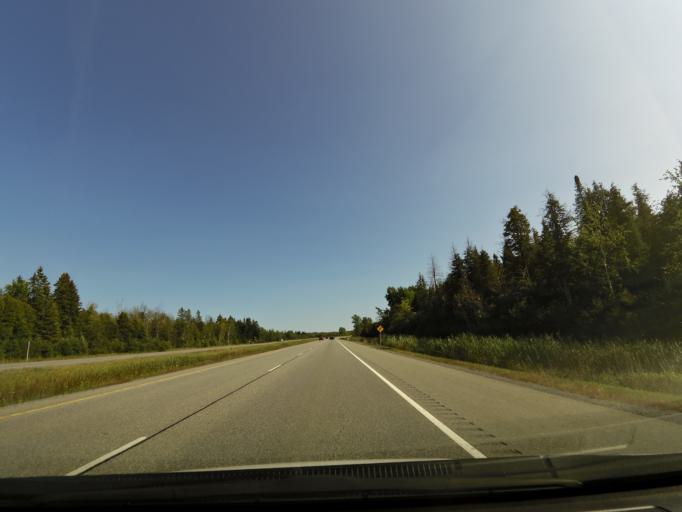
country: CA
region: Ontario
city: Bells Corners
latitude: 45.2950
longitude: -76.0197
